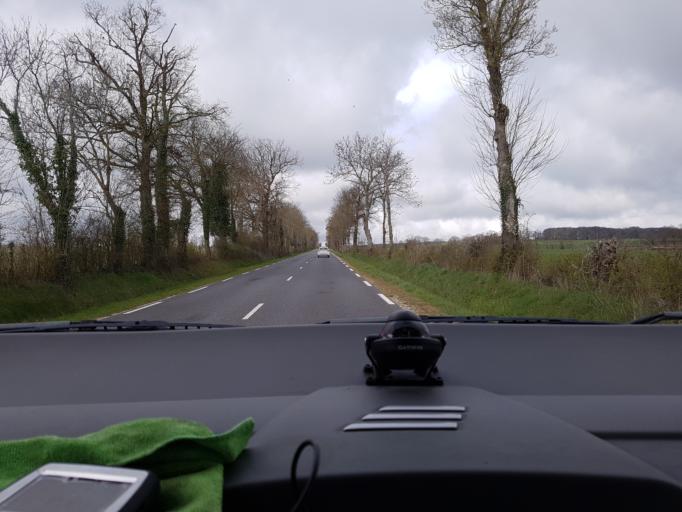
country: FR
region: Midi-Pyrenees
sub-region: Departement de l'Aveyron
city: Druelle
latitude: 44.3696
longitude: 2.4916
